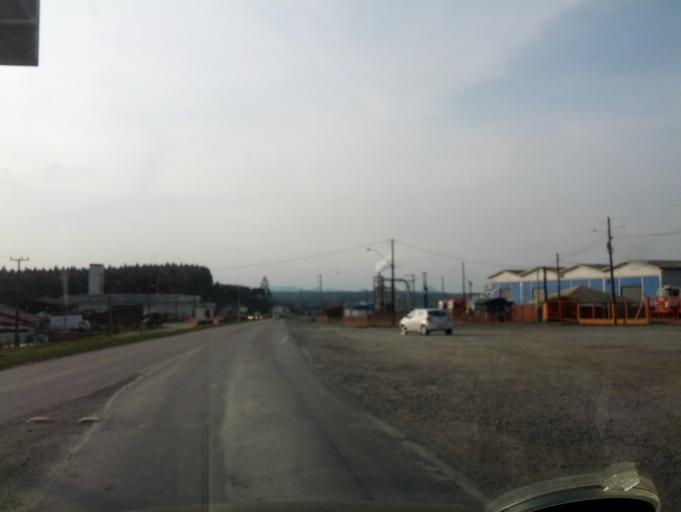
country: BR
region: Santa Catarina
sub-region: Otacilio Costa
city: Otacilio Costa
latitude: -27.4802
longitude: -50.1186
